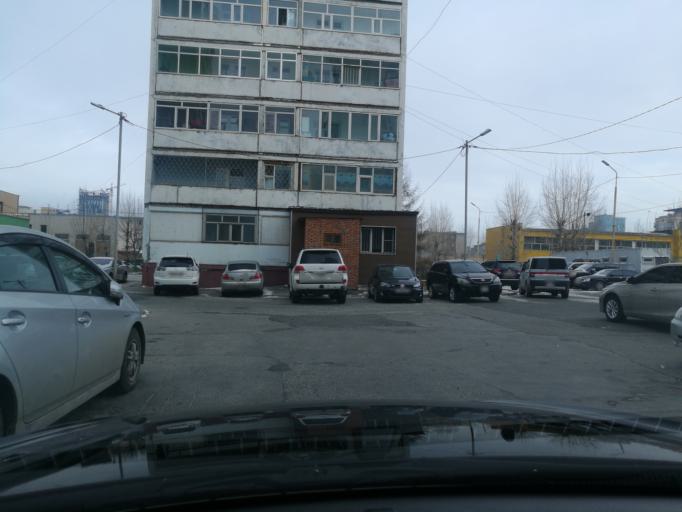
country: MN
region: Ulaanbaatar
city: Ulaanbaatar
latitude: 47.9096
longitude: 106.8967
